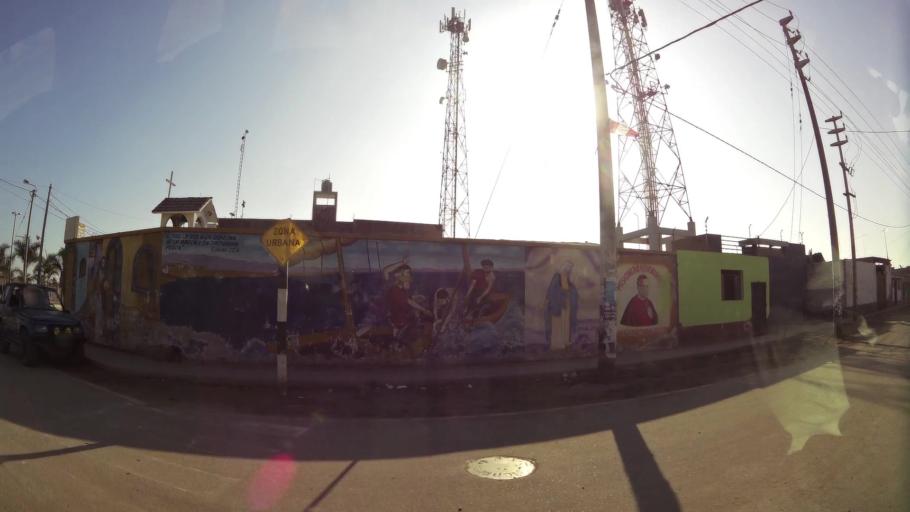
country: PE
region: Ica
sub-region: Provincia de Chincha
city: Chincha Baja
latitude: -13.4577
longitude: -76.1821
